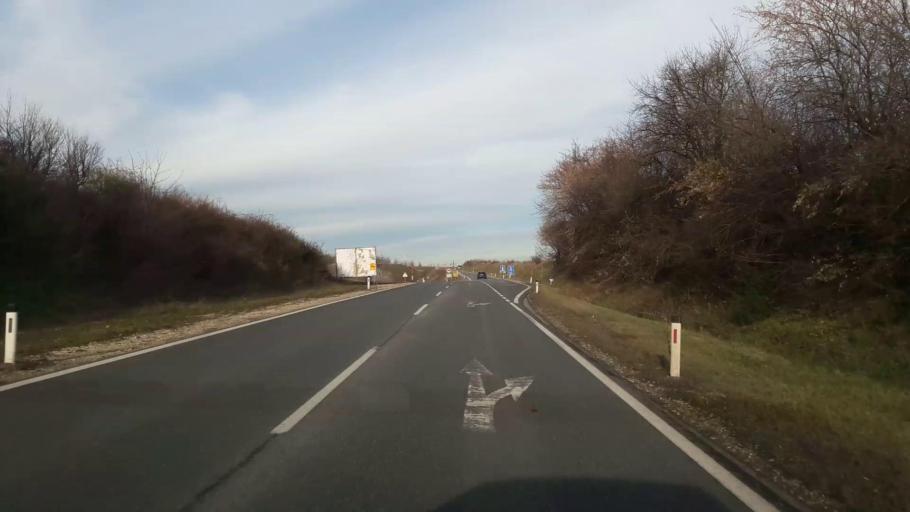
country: AT
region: Lower Austria
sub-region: Politischer Bezirk Mistelbach
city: Gaweinstal
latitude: 48.4920
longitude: 16.5970
